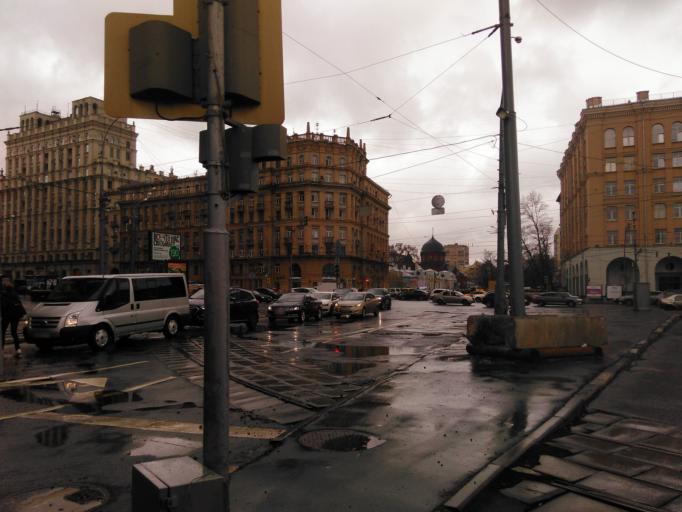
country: RU
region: Moscow
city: Zamoskvorech'ye
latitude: 55.7305
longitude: 37.6367
